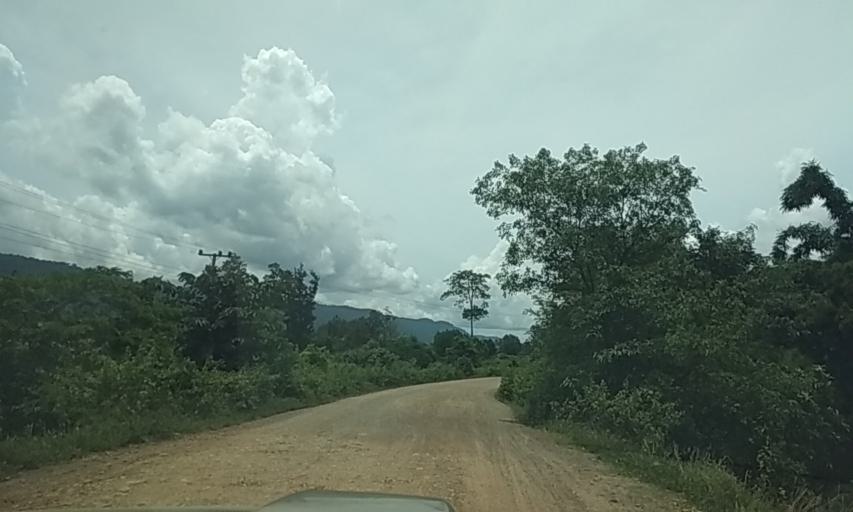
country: LA
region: Bolikhamxai
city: Ban Nahin
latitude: 18.1434
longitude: 104.7556
